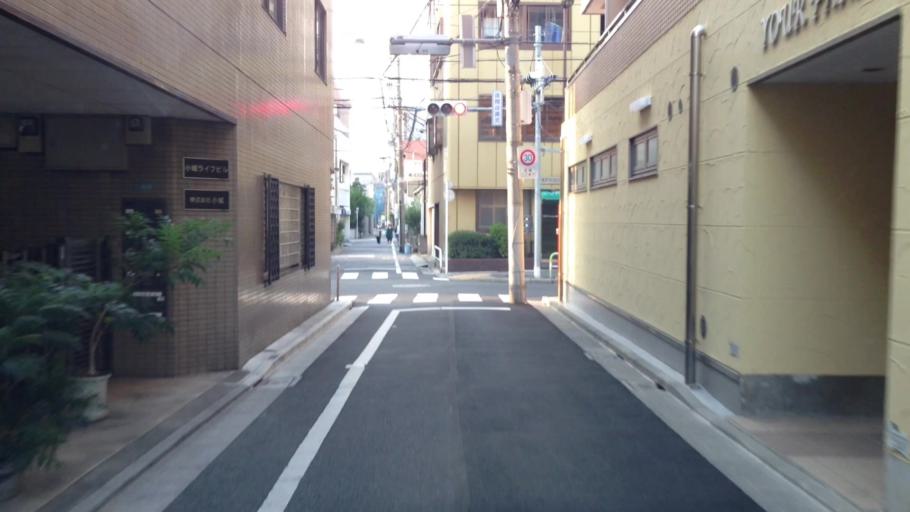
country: JP
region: Saitama
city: Soka
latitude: 35.7336
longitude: 139.7965
